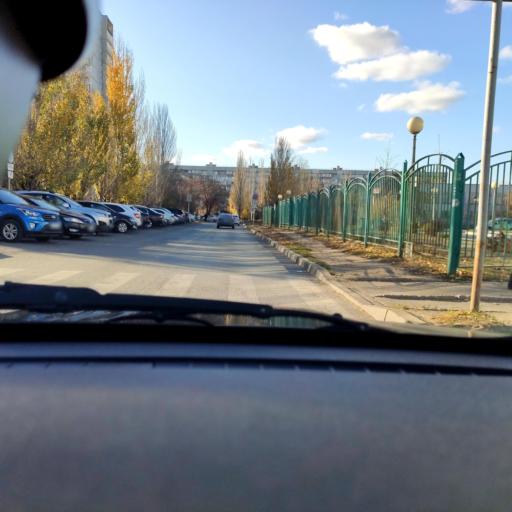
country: RU
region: Samara
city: Tol'yatti
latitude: 53.5370
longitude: 49.3367
